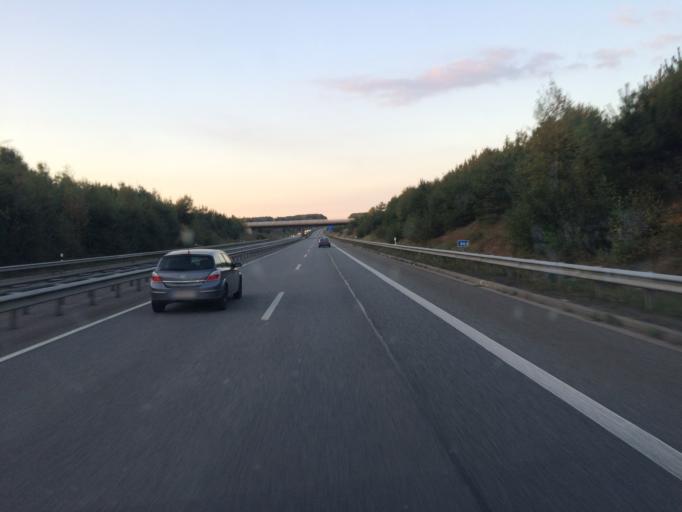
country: DE
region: Rheinland-Pfalz
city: Mehlingen
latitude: 49.4976
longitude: 7.8432
